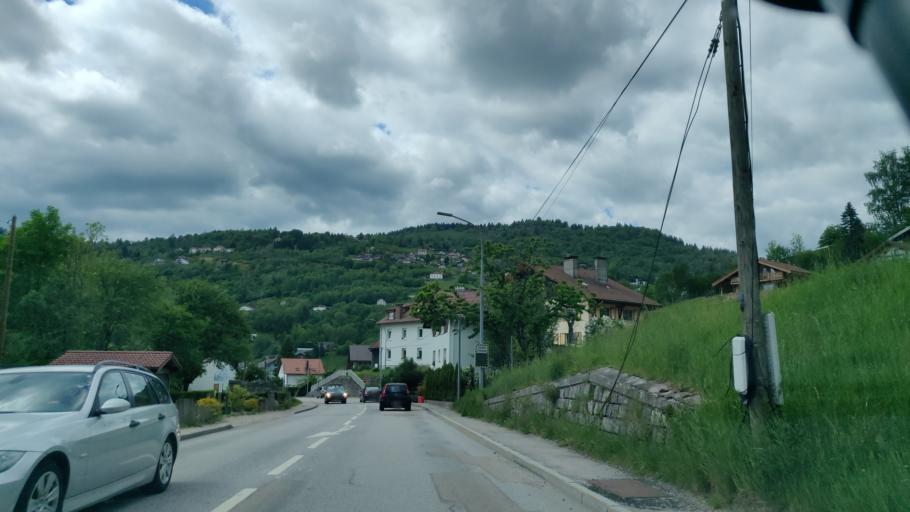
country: FR
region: Lorraine
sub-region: Departement des Vosges
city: La Bresse
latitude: 48.0056
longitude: 6.8868
